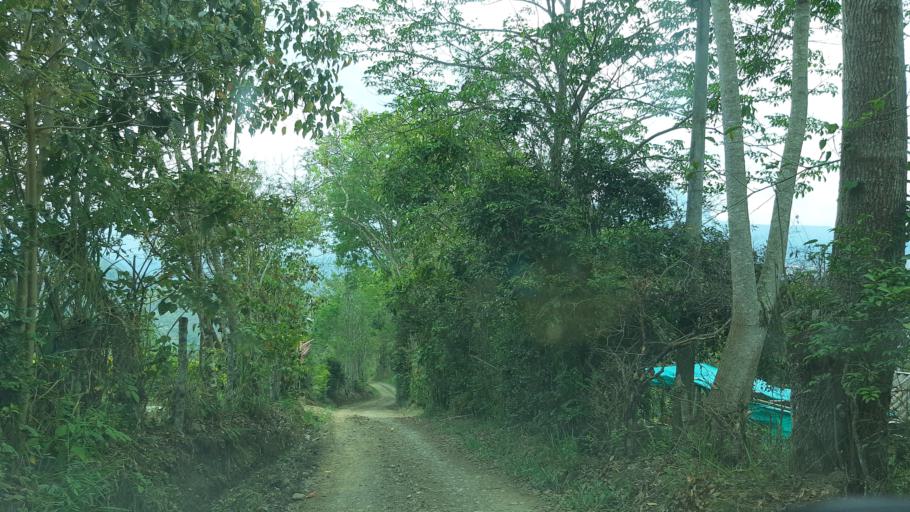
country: CO
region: Boyaca
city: Garagoa
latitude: 5.0829
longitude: -73.3916
